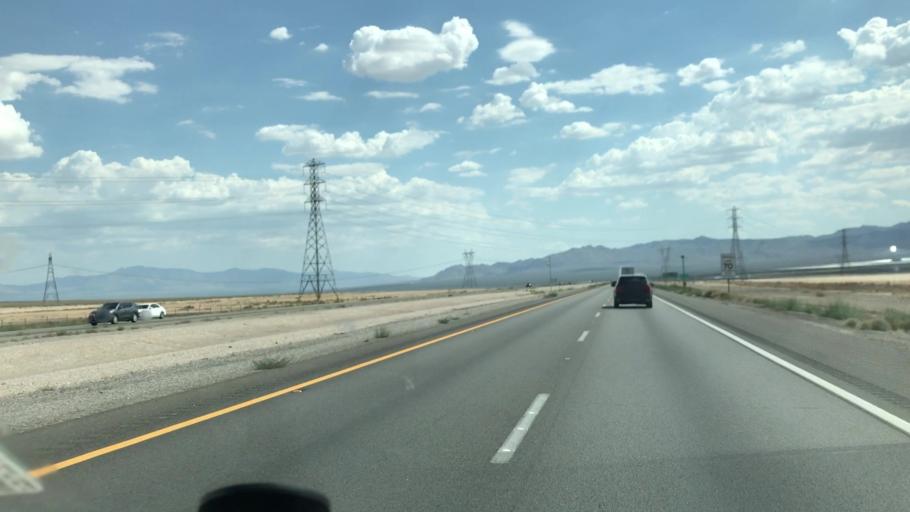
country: US
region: Nevada
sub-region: Clark County
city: Sandy Valley
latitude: 35.6043
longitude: -115.3929
